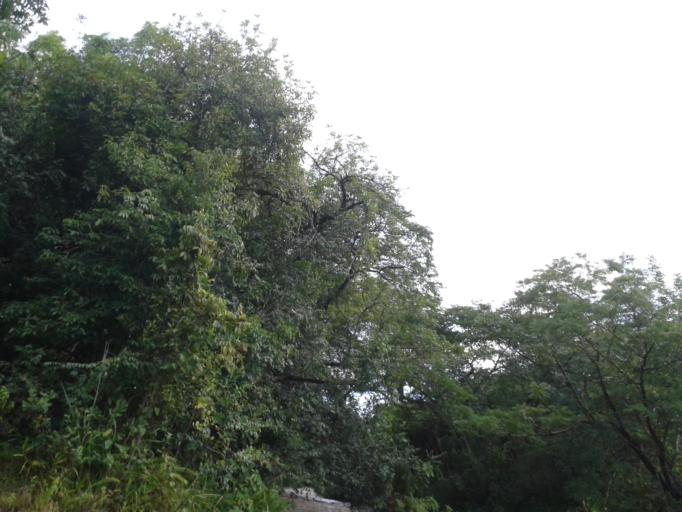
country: BR
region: Minas Gerais
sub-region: Ituiutaba
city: Ituiutaba
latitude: -18.9336
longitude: -49.3347
